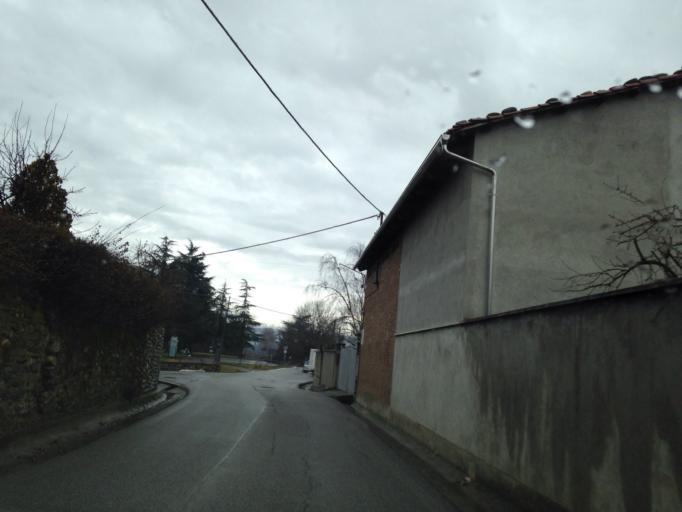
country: IT
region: Piedmont
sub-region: Provincia di Vercelli
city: Moncrivello
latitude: 45.3351
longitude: 7.9947
